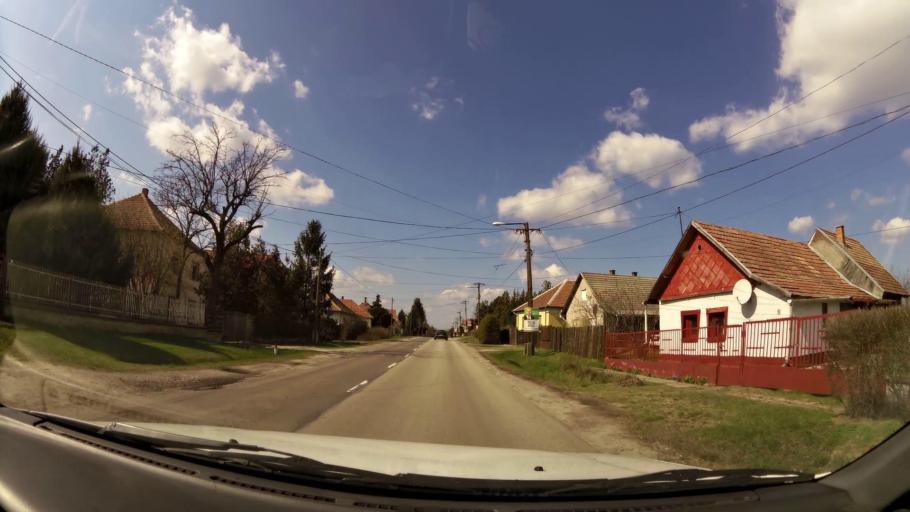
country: HU
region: Pest
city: Farmos
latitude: 47.3539
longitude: 19.8554
